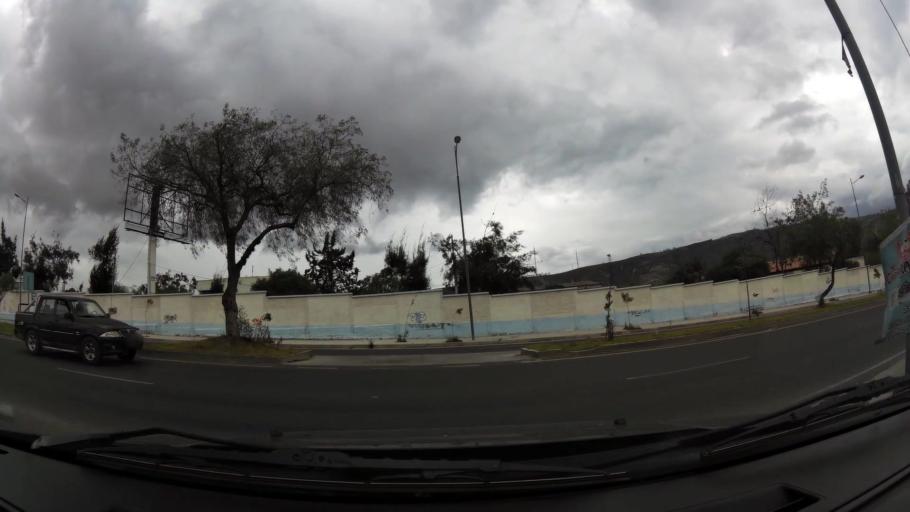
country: EC
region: Pichincha
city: Quito
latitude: -0.0084
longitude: -78.4531
